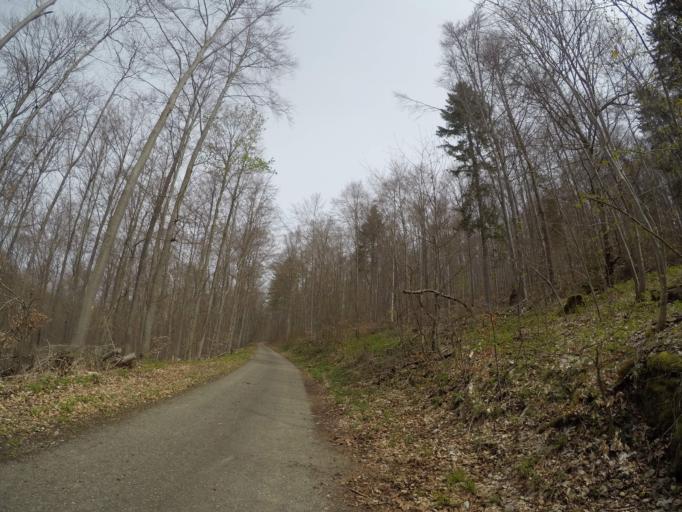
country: DE
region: Baden-Wuerttemberg
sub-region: Regierungsbezirk Stuttgart
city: Neidlingen
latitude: 48.5368
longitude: 9.5613
